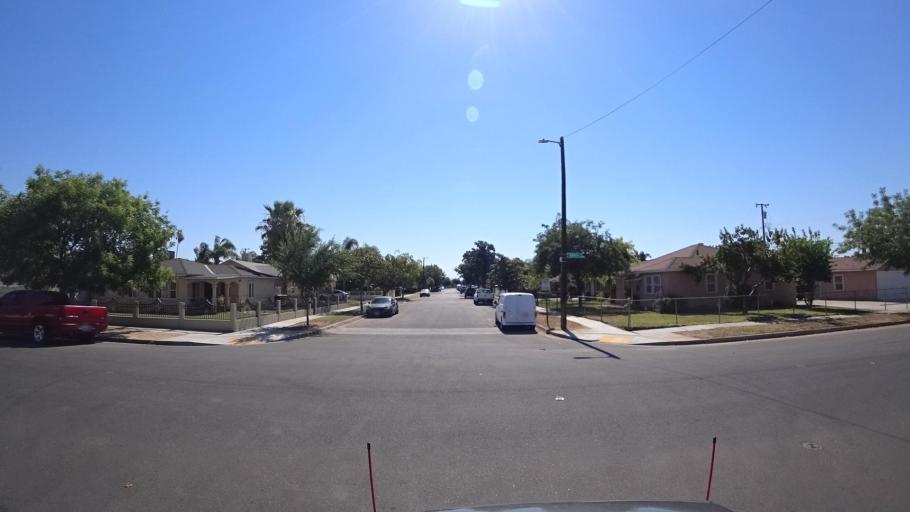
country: US
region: California
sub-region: Fresno County
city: Fresno
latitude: 36.7241
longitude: -119.7615
